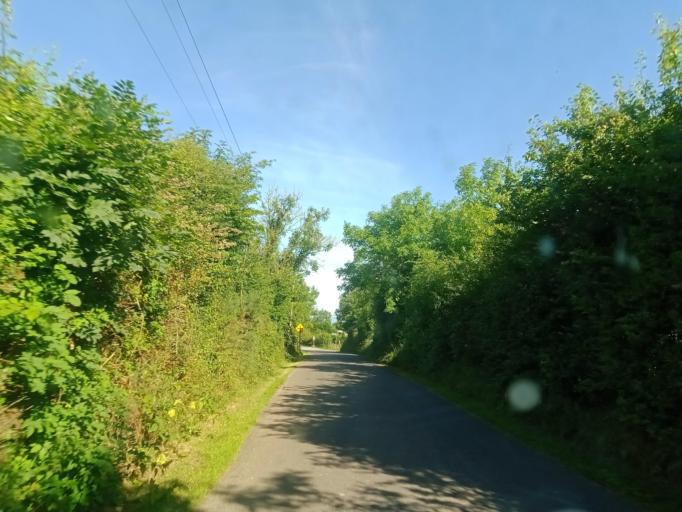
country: IE
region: Leinster
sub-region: Kilkenny
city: Ballyragget
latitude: 52.7827
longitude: -7.4182
